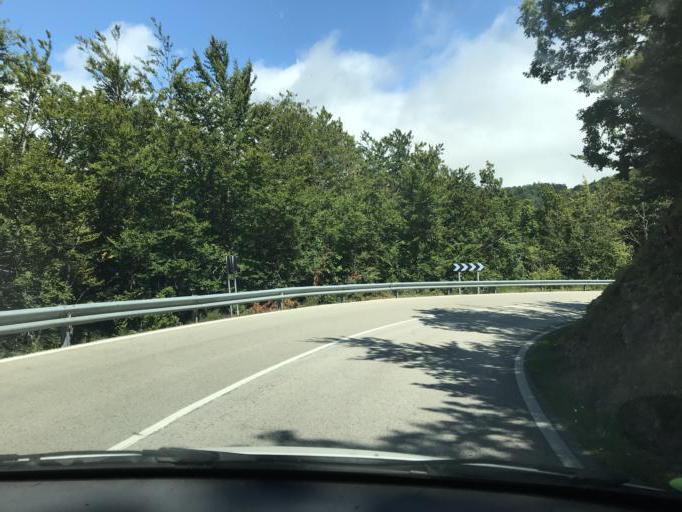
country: ES
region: Cantabria
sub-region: Provincia de Cantabria
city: Cabezon de Liebana
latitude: 43.0684
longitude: -4.4798
